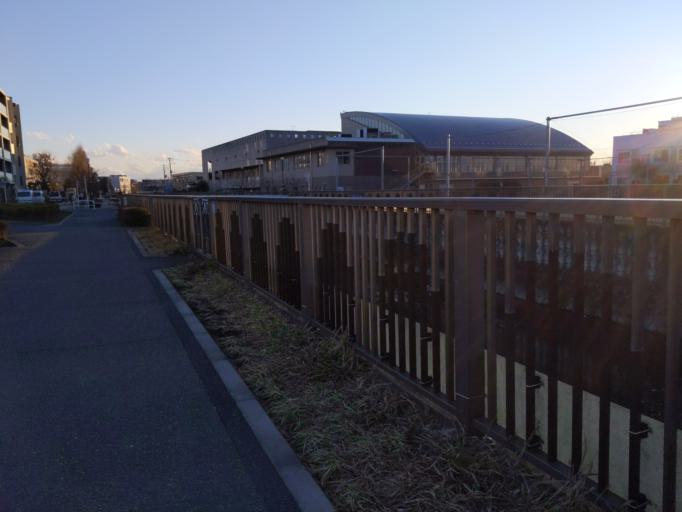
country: JP
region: Tokyo
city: Chofugaoka
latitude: 35.6236
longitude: 139.6132
